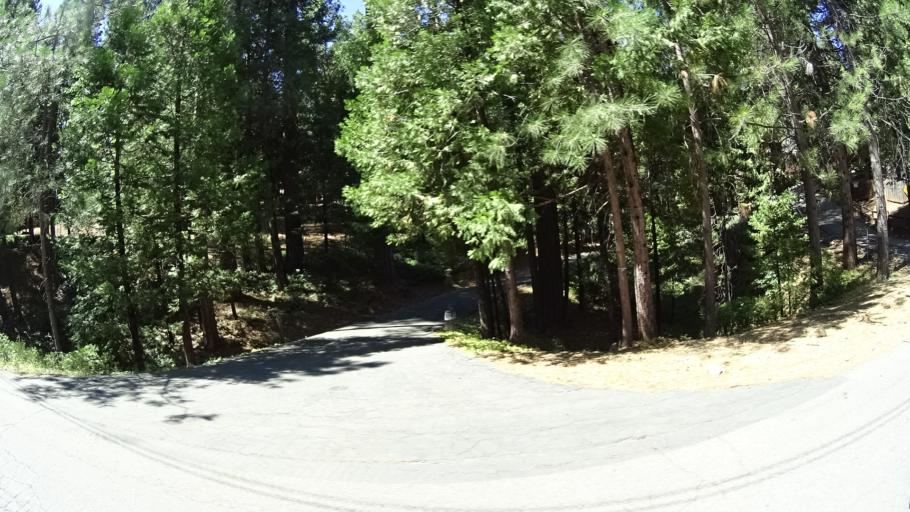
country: US
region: California
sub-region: Calaveras County
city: Arnold
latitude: 38.2262
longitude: -120.3404
